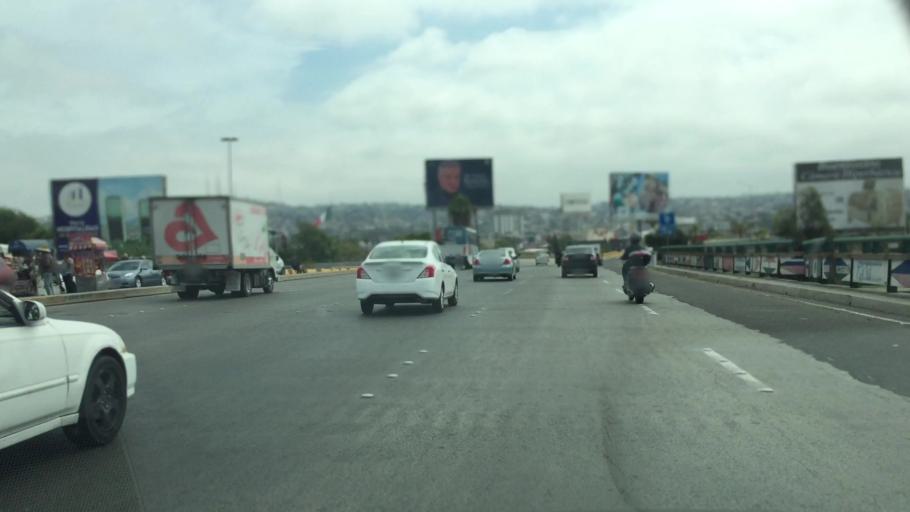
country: MX
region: Baja California
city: Tijuana
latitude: 32.5364
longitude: -117.0285
